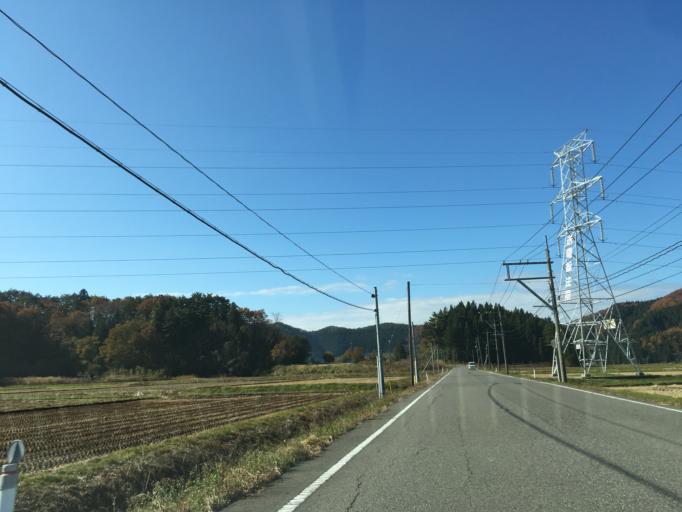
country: JP
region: Fukushima
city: Inawashiro
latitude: 37.3994
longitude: 140.0929
